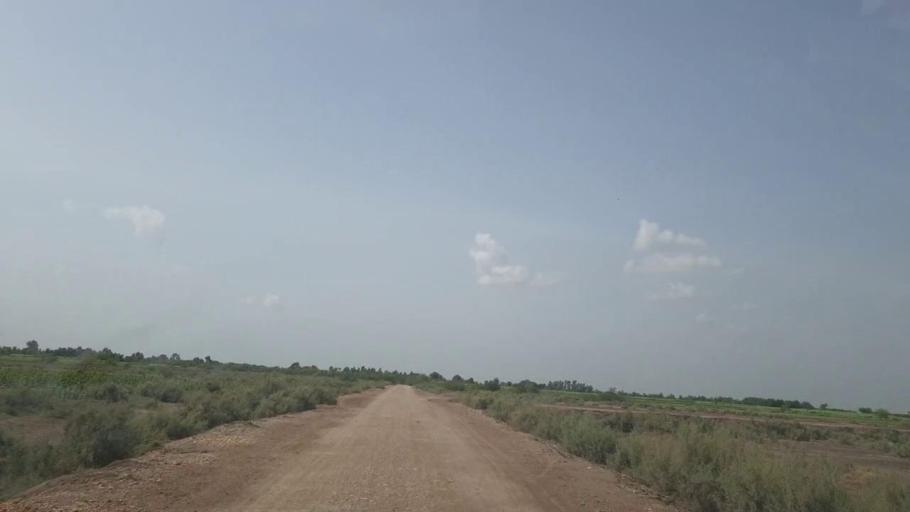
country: PK
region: Sindh
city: Tando Bago
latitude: 24.7755
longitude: 69.1306
